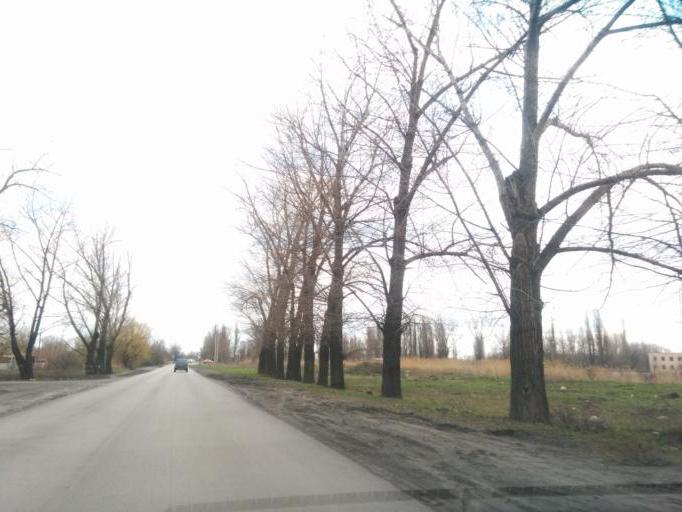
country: RU
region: Rostov
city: Shakhty
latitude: 47.6810
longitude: 40.2847
